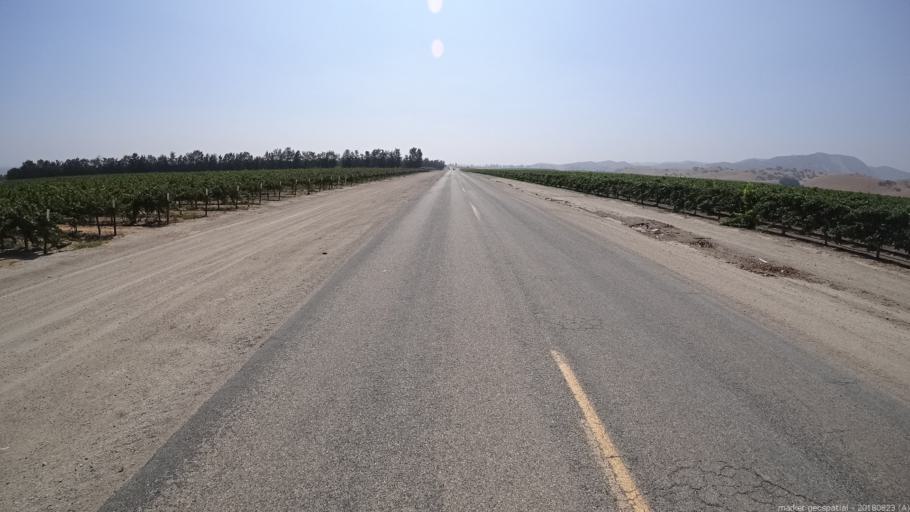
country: US
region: California
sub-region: Monterey County
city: King City
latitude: 36.2492
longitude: -121.1944
